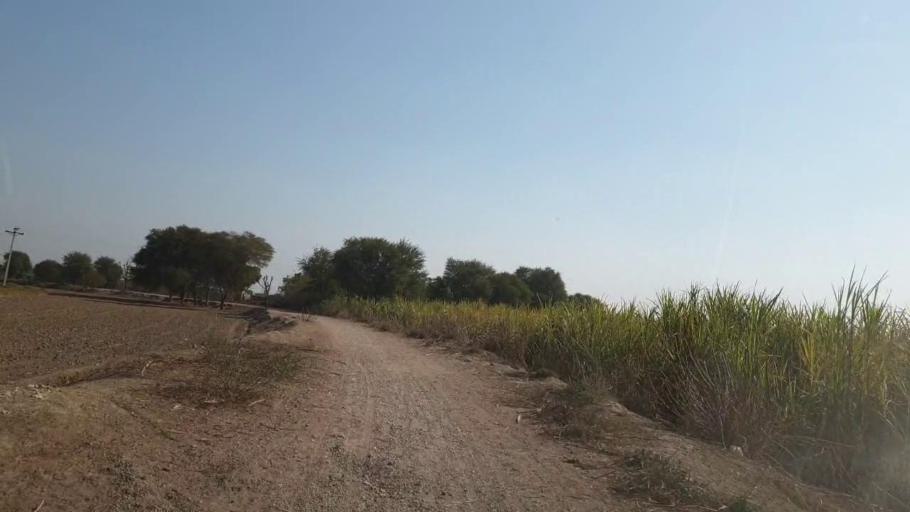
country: PK
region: Sindh
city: Tando Jam
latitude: 25.4995
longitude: 68.5124
